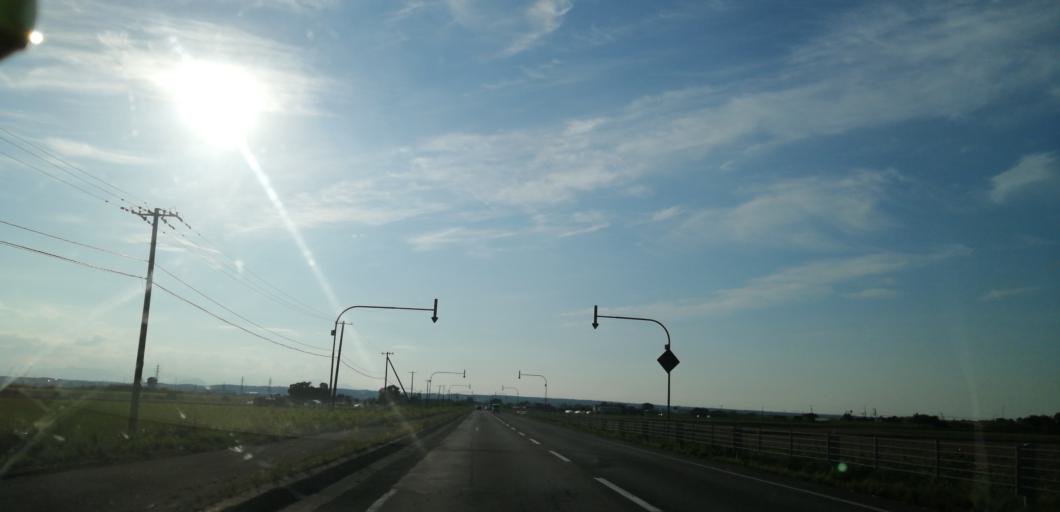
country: JP
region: Hokkaido
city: Kitahiroshima
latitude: 42.9916
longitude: 141.6033
